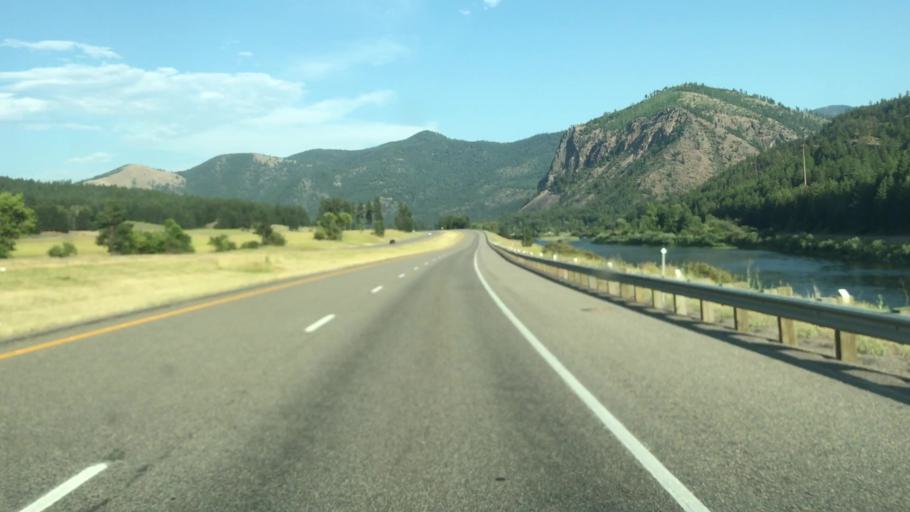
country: US
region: Montana
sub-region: Missoula County
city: Frenchtown
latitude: 46.9993
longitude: -114.4679
